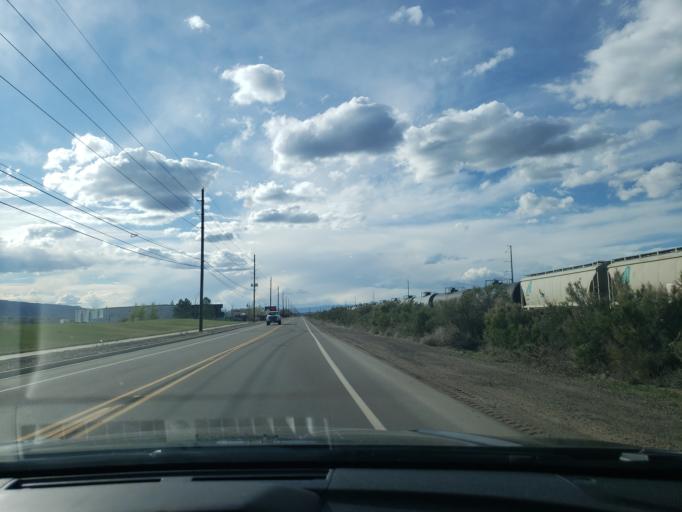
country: US
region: Colorado
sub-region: Mesa County
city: Redlands
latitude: 39.1003
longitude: -108.6274
